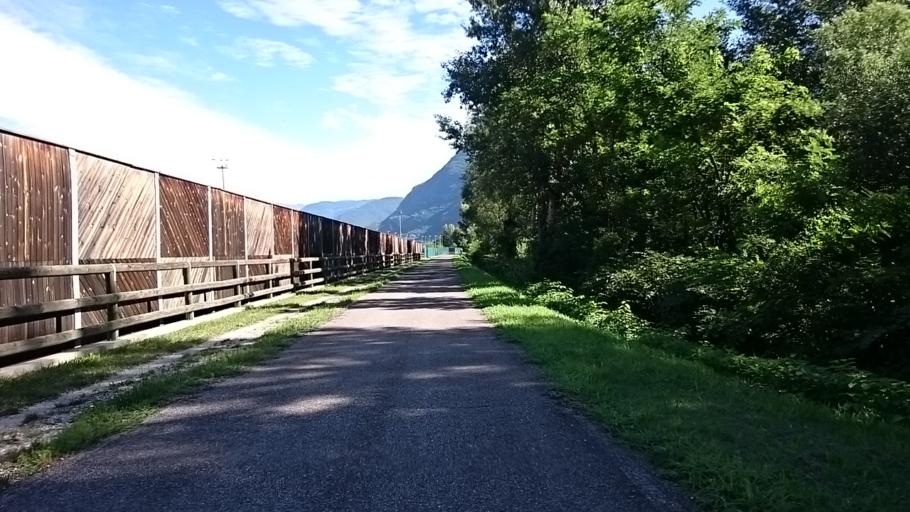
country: IT
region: Trentino-Alto Adige
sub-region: Bolzano
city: Vadena
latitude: 46.4314
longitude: 11.3120
